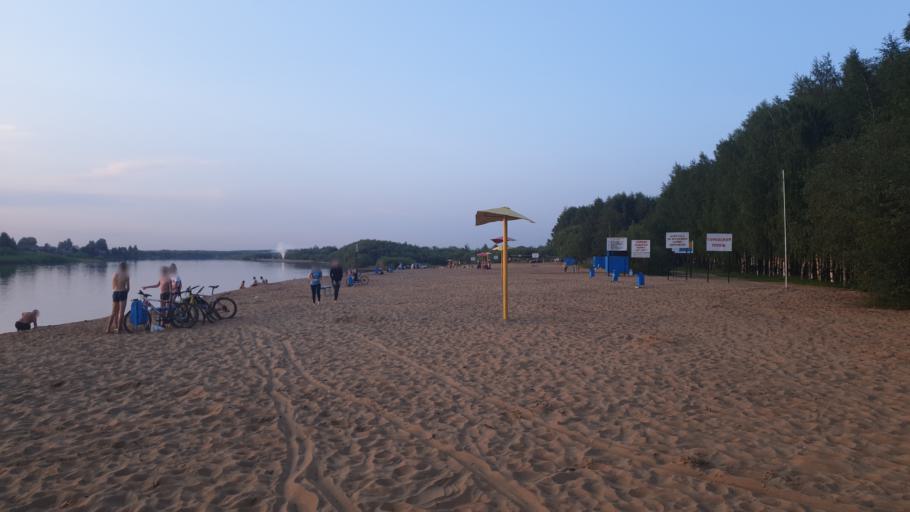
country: RU
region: Komi Republic
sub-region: Syktyvdinskiy Rayon
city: Syktyvkar
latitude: 61.6712
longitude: 50.8604
